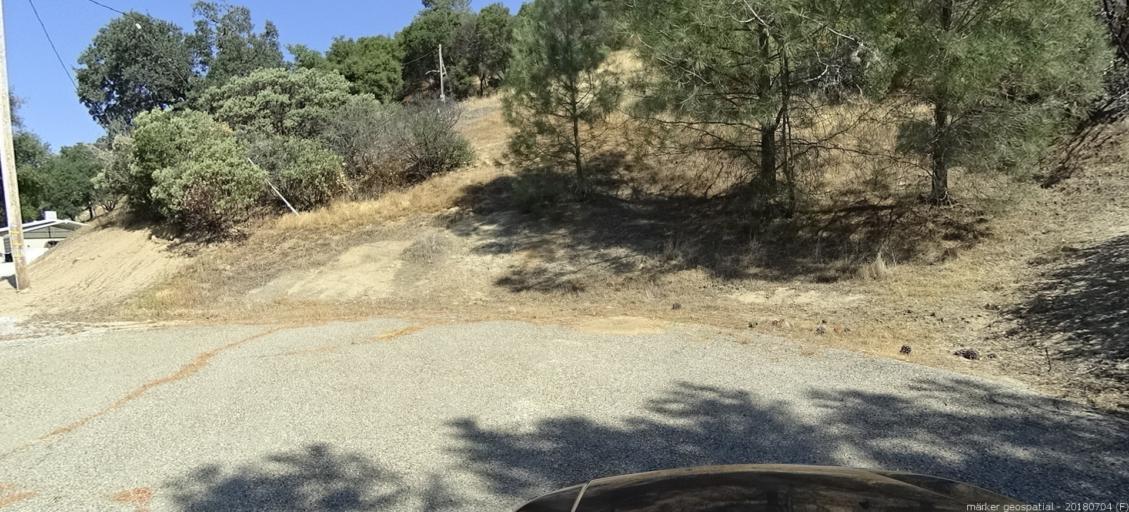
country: US
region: California
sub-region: Fresno County
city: Auberry
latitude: 37.1856
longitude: -119.4602
